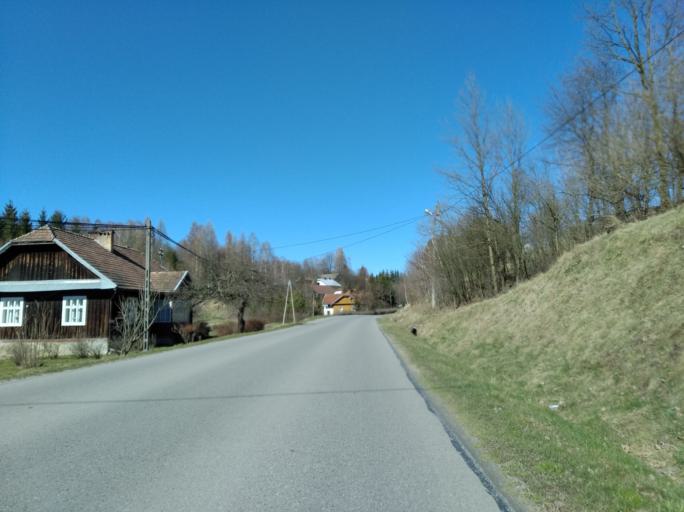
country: PL
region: Subcarpathian Voivodeship
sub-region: Powiat strzyzowski
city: Wisniowa
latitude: 49.8914
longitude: 21.6648
